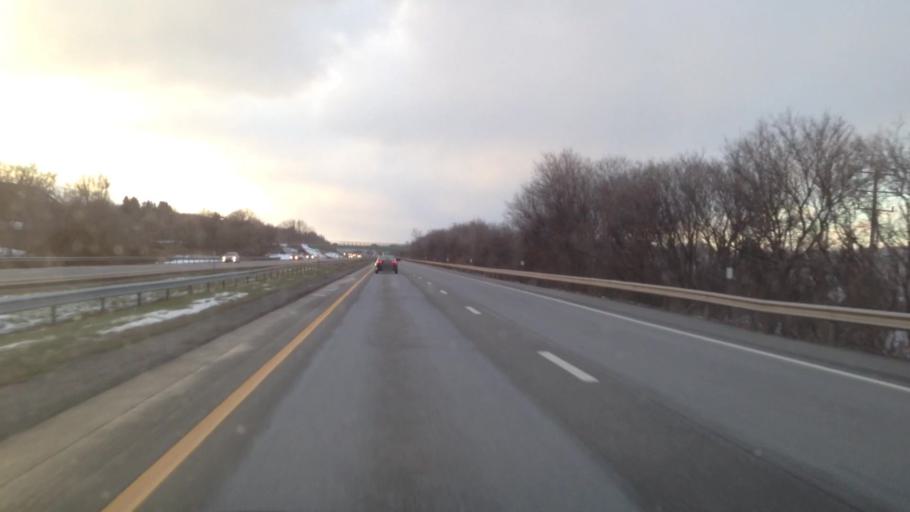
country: US
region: New York
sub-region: Herkimer County
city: Herkimer
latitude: 43.0143
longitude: -74.9408
